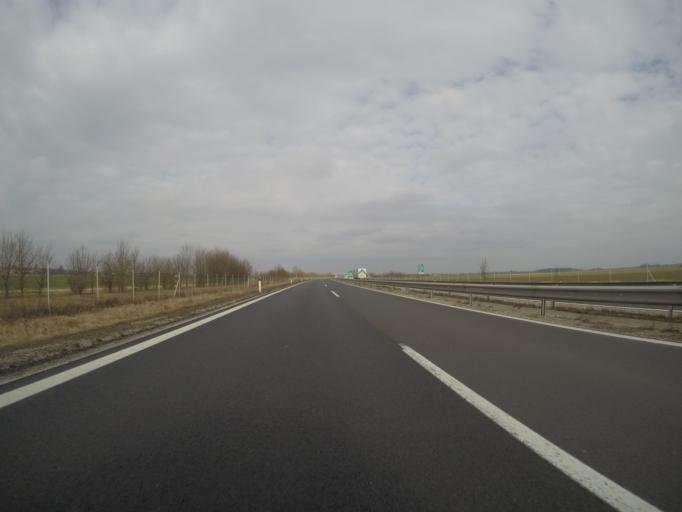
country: SI
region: Murska Sobota
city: Krog
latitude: 46.6256
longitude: 16.1375
